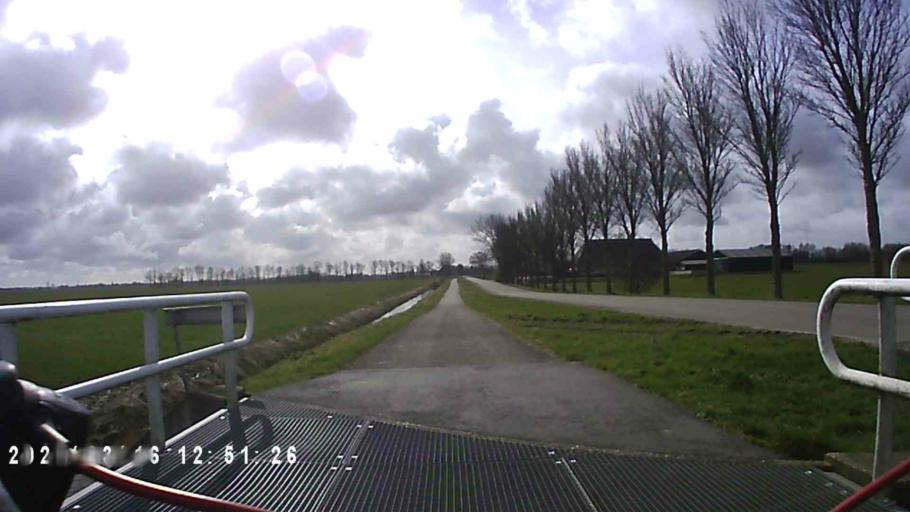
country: NL
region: Friesland
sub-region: Gemeente Het Bildt
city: Sint Annaparochie
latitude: 53.2598
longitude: 5.6797
